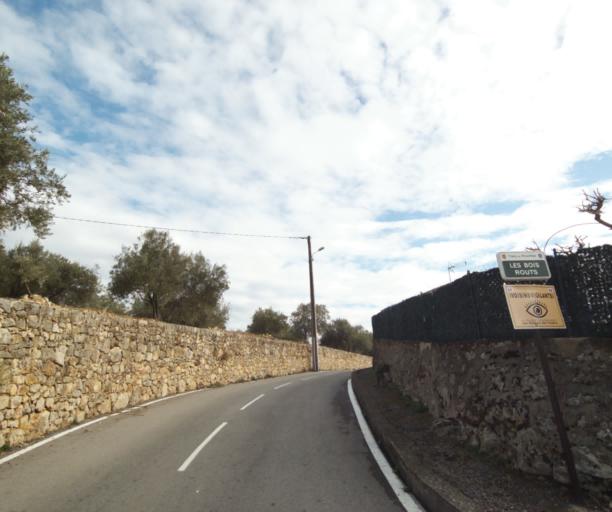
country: FR
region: Provence-Alpes-Cote d'Azur
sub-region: Departement du Var
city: Trans-en-Provence
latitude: 43.5031
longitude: 6.4916
